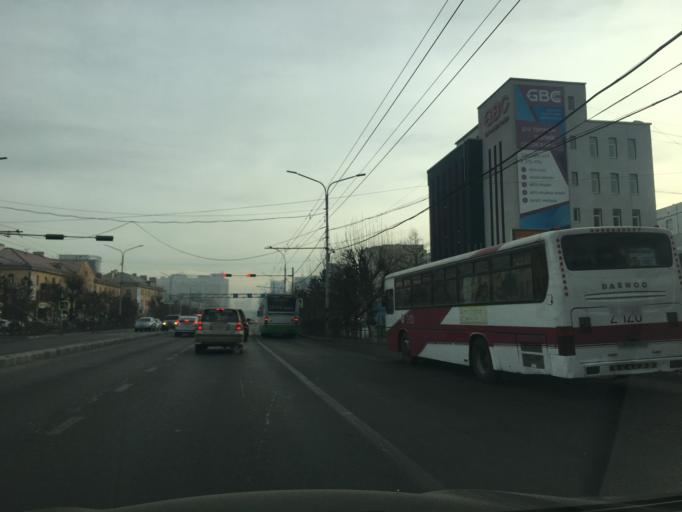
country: MN
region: Ulaanbaatar
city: Ulaanbaatar
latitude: 47.9145
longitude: 106.8801
